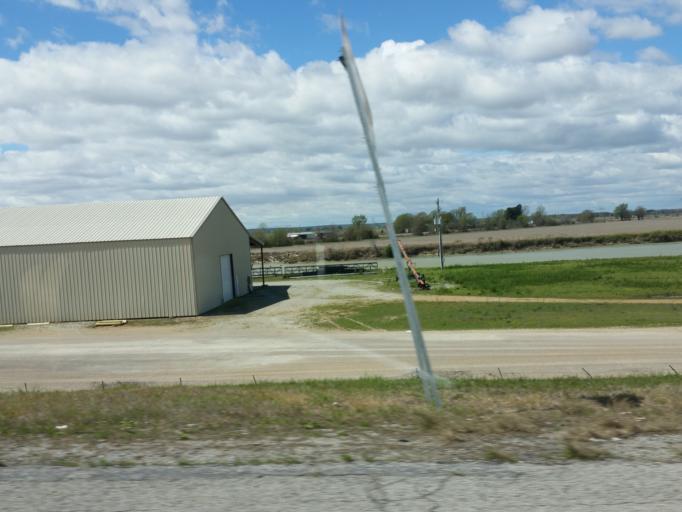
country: US
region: Arkansas
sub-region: Craighead County
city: Bay
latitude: 35.7594
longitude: -90.5779
